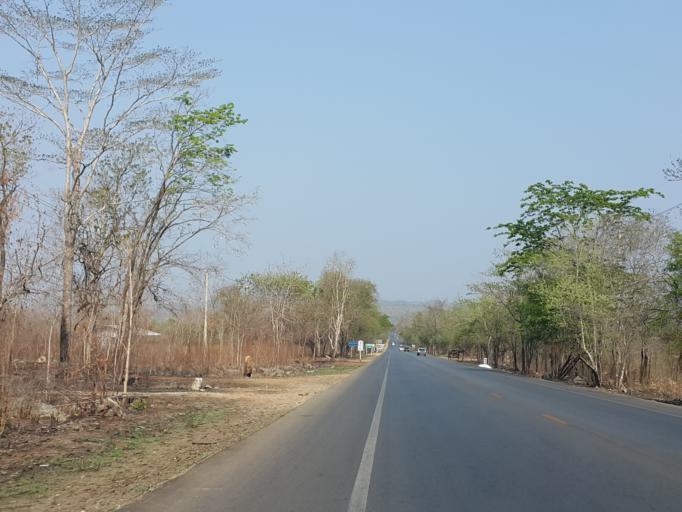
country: TH
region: Kanchanaburi
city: Sai Yok
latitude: 14.0955
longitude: 99.2553
